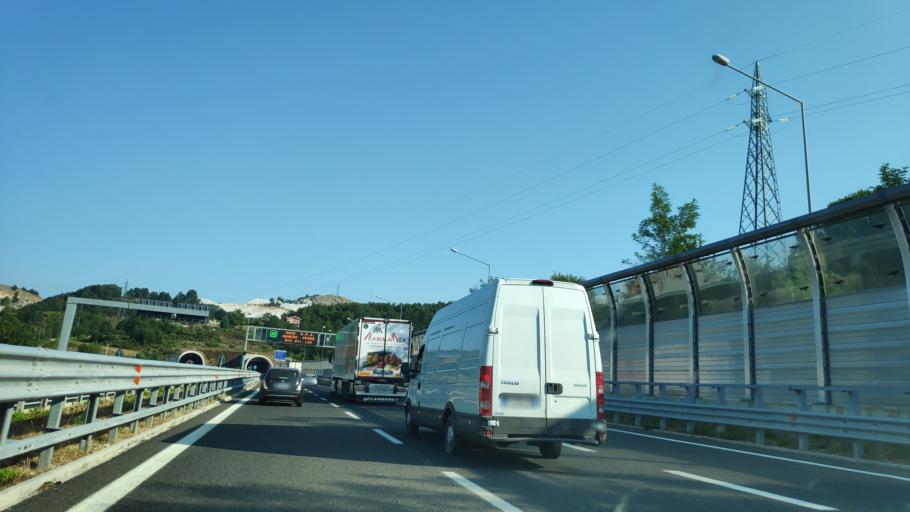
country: IT
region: Basilicate
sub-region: Provincia di Potenza
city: Lagonegro
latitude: 40.1365
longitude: 15.7599
